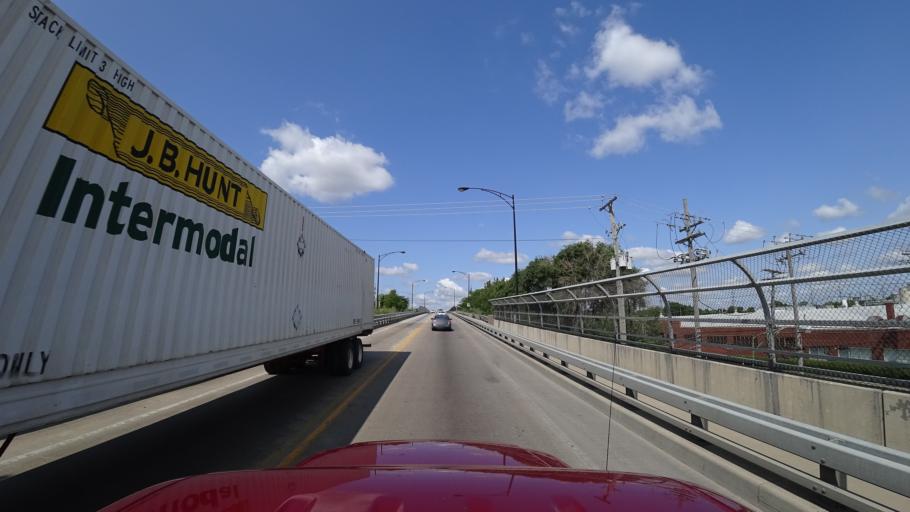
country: US
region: Illinois
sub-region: Cook County
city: Cicero
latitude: 41.8368
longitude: -87.7361
